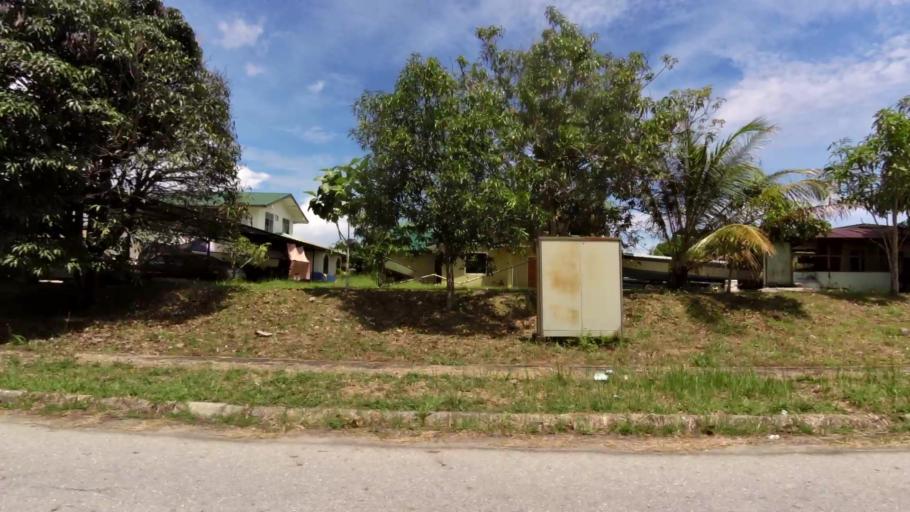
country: BN
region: Brunei and Muara
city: Bandar Seri Begawan
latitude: 4.9581
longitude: 114.9067
